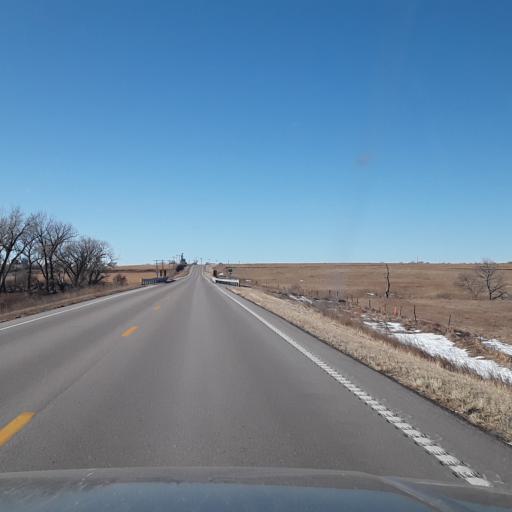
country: US
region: Nebraska
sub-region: Dawson County
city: Gothenburg
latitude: 40.7039
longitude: -100.1888
